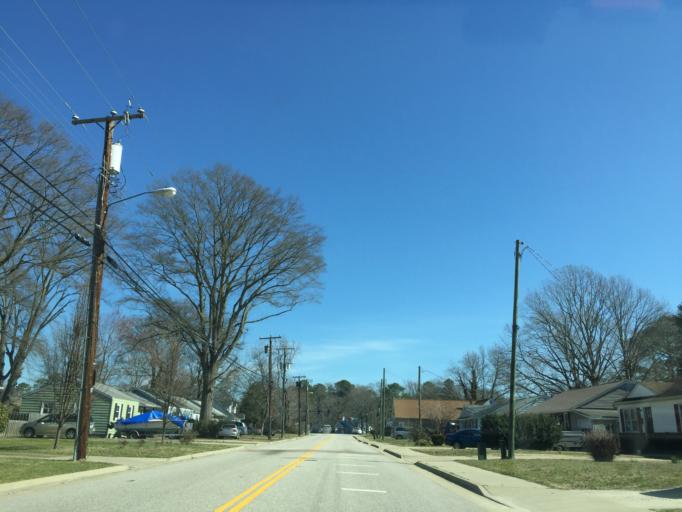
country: US
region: Virginia
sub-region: City of Newport News
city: Newport News
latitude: 37.0792
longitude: -76.4993
